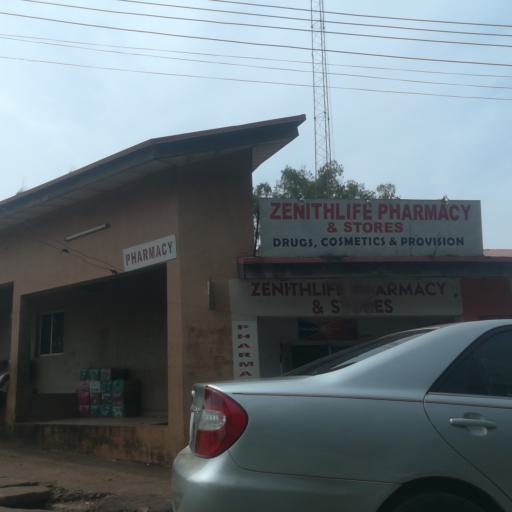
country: NG
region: Plateau
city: Jos
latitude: 9.8778
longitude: 8.8733
